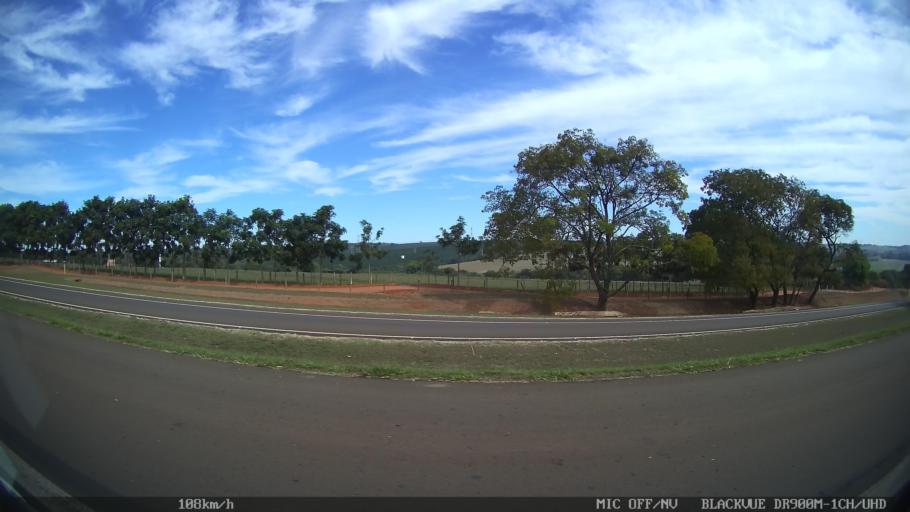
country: BR
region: Sao Paulo
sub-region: Matao
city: Matao
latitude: -21.5938
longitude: -48.4396
